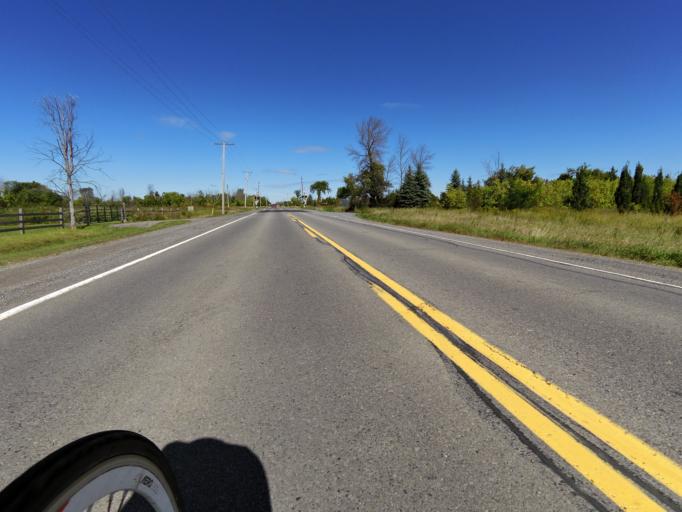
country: CA
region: Ontario
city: Bells Corners
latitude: 45.1953
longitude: -75.8174
